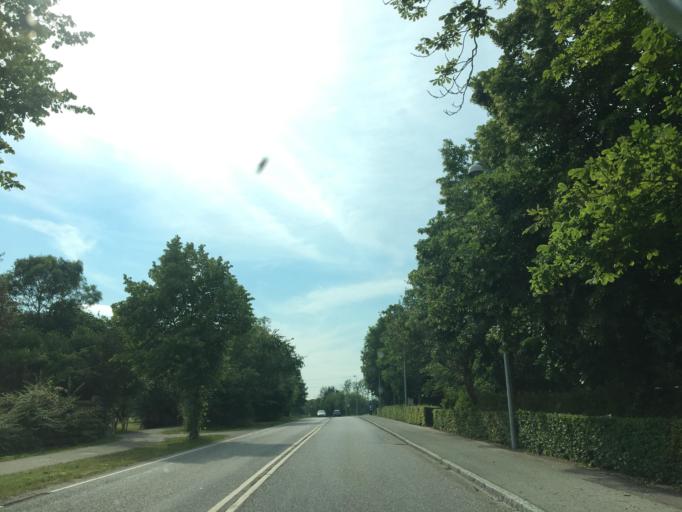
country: DK
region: Zealand
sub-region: Greve Kommune
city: Tune
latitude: 55.5975
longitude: 12.2177
